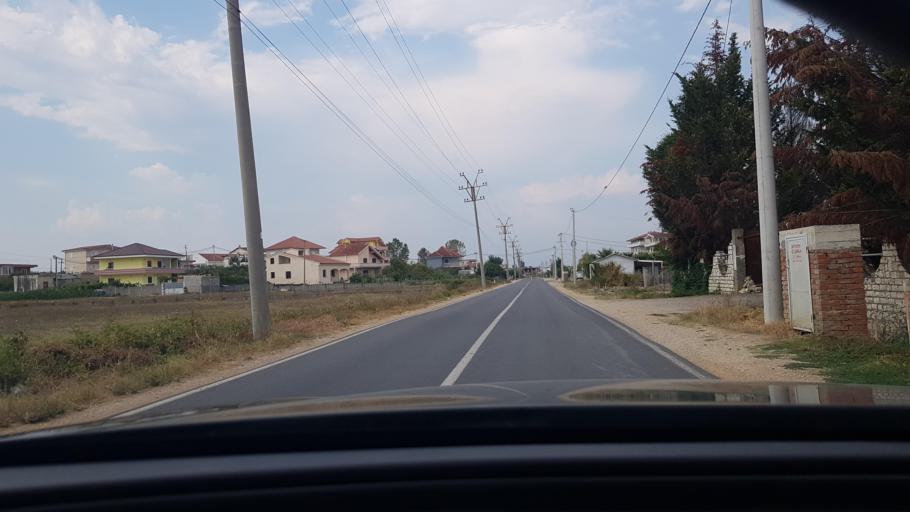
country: AL
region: Durres
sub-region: Rrethi i Durresit
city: Sukth
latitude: 41.4082
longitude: 19.5468
